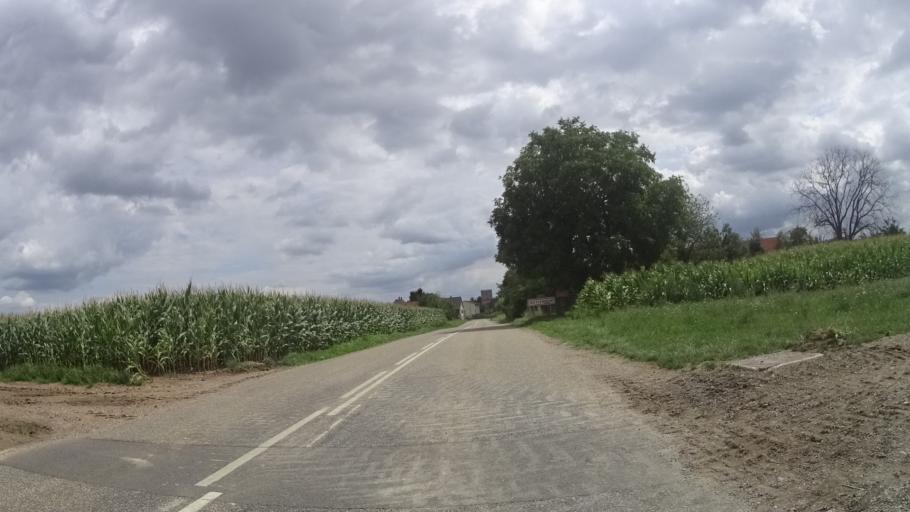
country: FR
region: Alsace
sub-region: Departement du Bas-Rhin
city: Hoerdt
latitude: 48.7209
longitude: 7.7797
